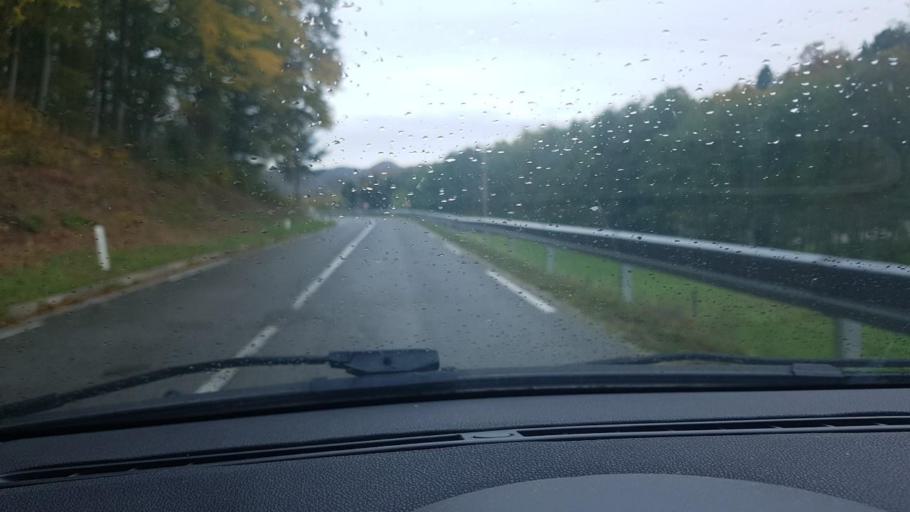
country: SI
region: Rogatec
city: Rogatec
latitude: 46.2478
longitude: 15.7000
